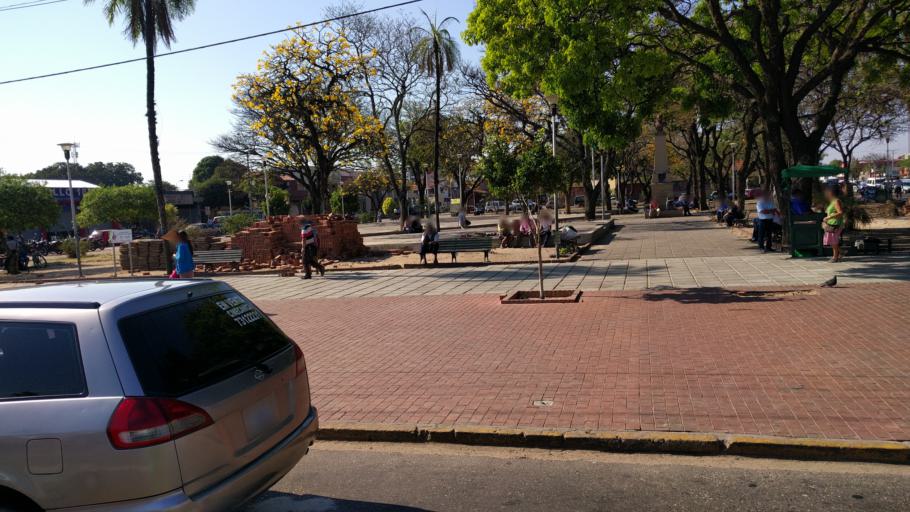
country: BO
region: Santa Cruz
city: Santa Cruz de la Sierra
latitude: -17.7979
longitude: -63.1924
